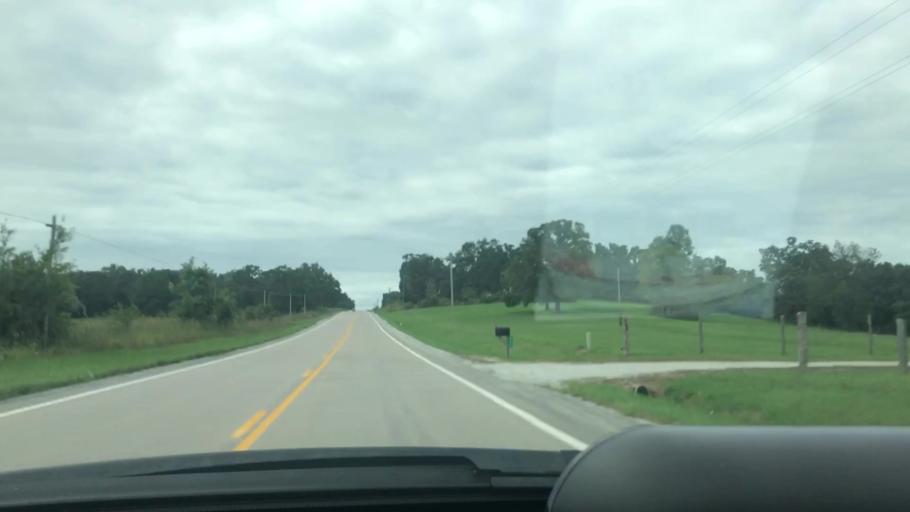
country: US
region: Missouri
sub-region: Benton County
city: Warsaw
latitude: 38.1368
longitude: -93.2835
